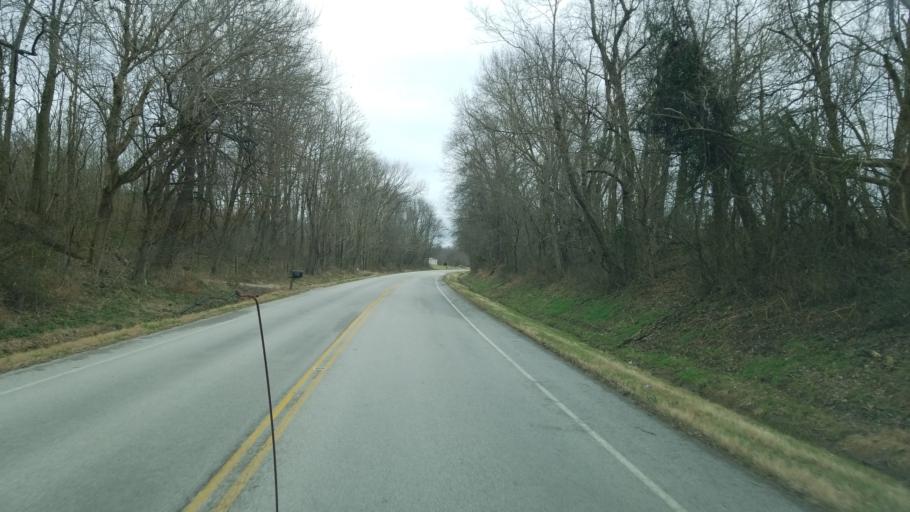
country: US
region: Kentucky
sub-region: Bracken County
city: Augusta
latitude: 38.7885
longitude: -83.9404
